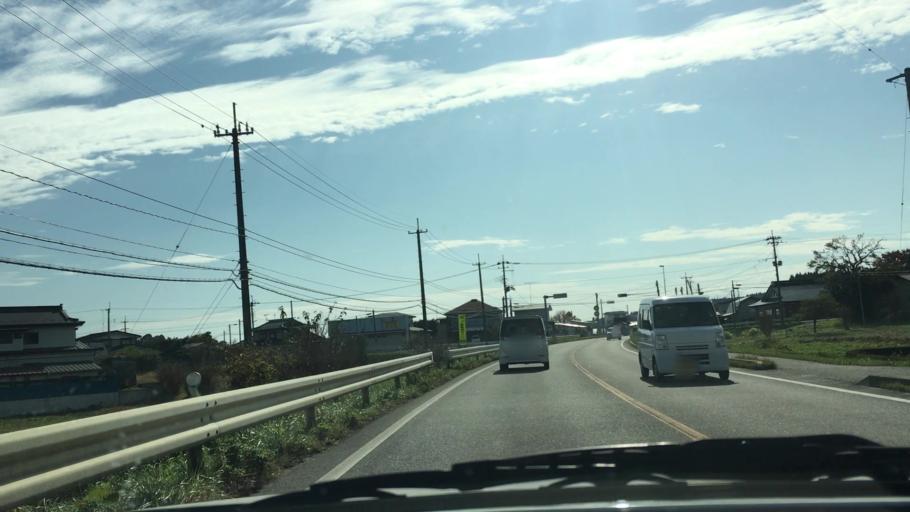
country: JP
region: Aomori
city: Hachinohe
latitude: 40.4242
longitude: 141.6979
